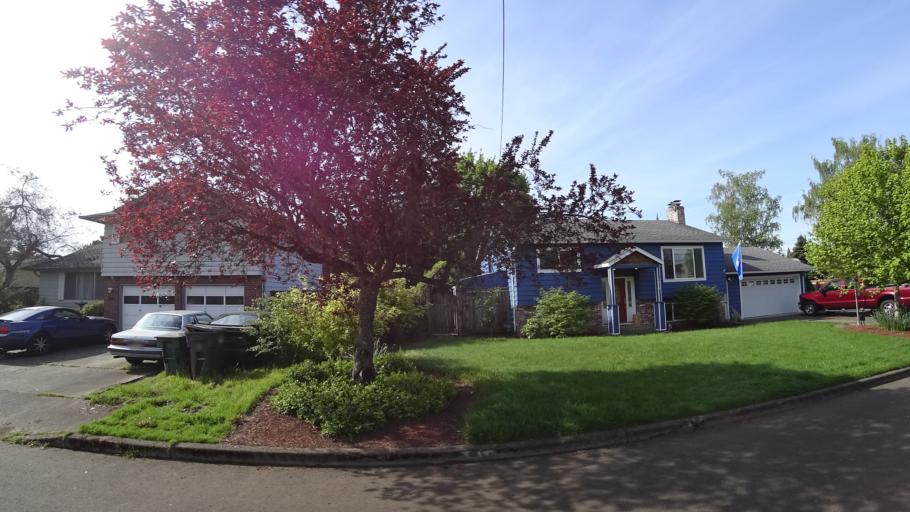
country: US
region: Oregon
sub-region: Washington County
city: Hillsboro
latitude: 45.5261
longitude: -122.9631
